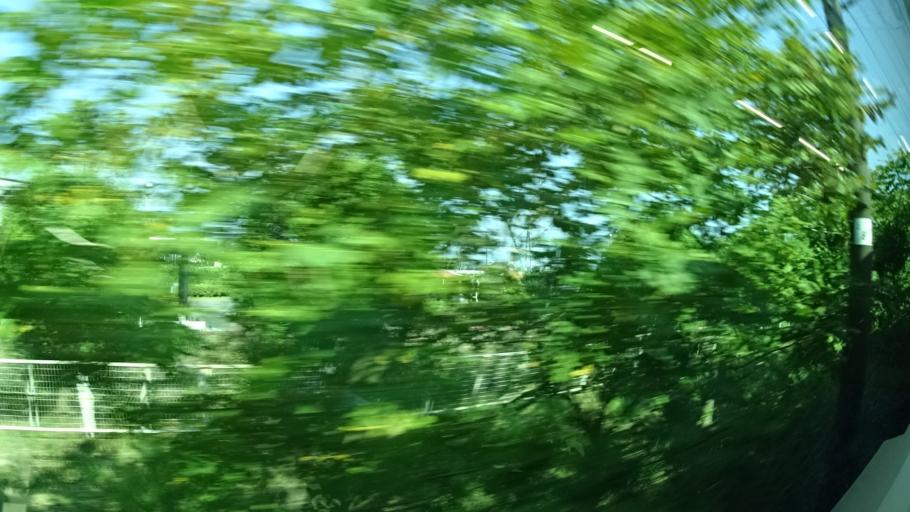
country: JP
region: Miyagi
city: Matsushima
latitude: 38.3906
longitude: 141.0660
